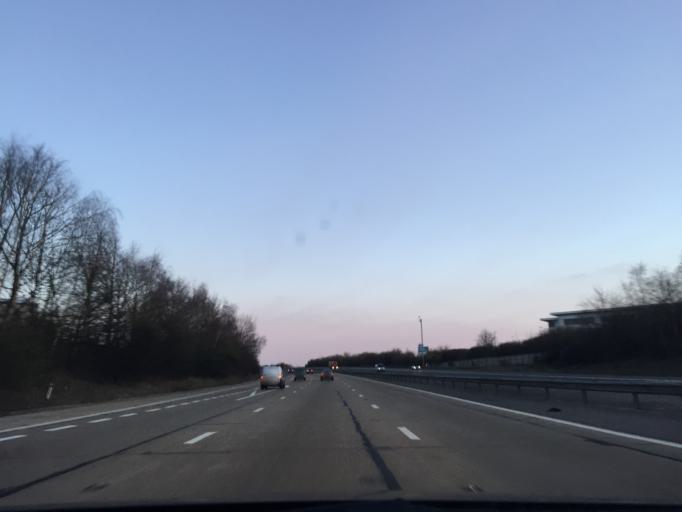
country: GB
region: England
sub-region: Hampshire
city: Eastleigh
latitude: 50.9440
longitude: -1.3636
